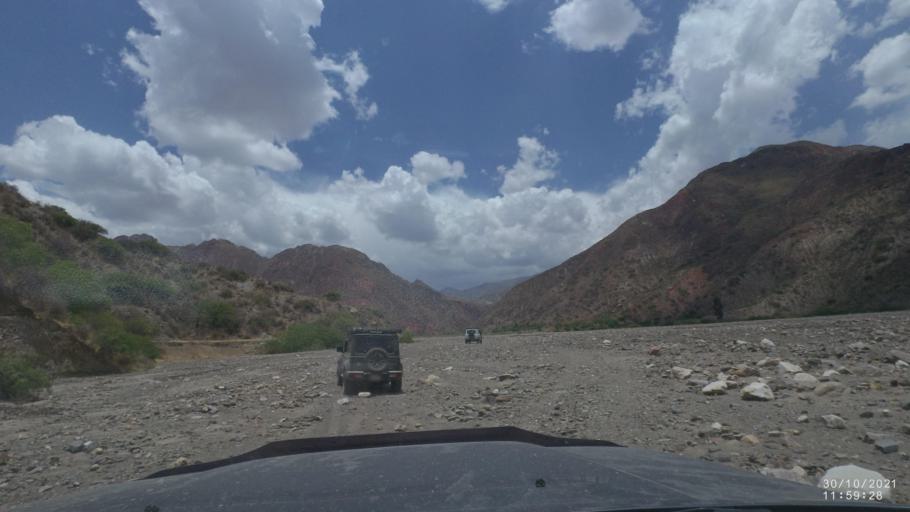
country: BO
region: Cochabamba
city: Colchani
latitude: -17.5254
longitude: -66.6185
